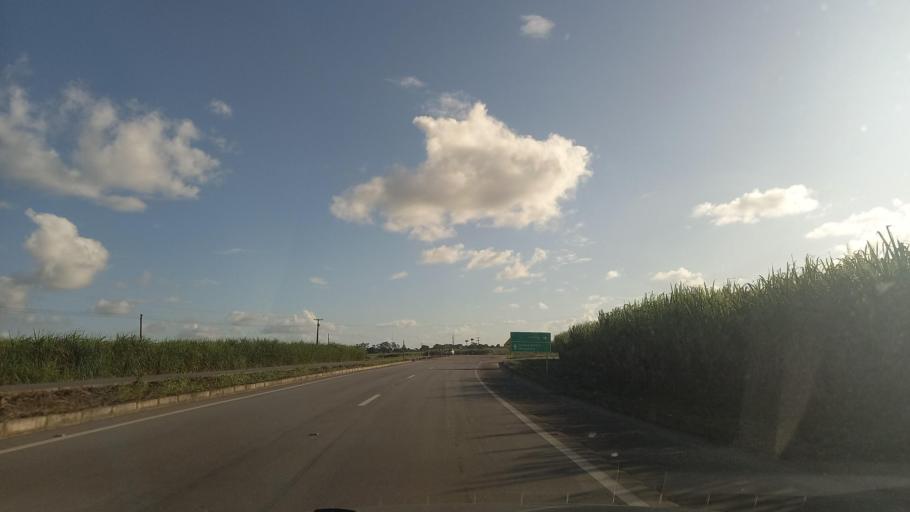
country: BR
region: Alagoas
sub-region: Sao Miguel Dos Campos
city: Sao Miguel dos Campos
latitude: -9.8033
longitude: -36.1992
